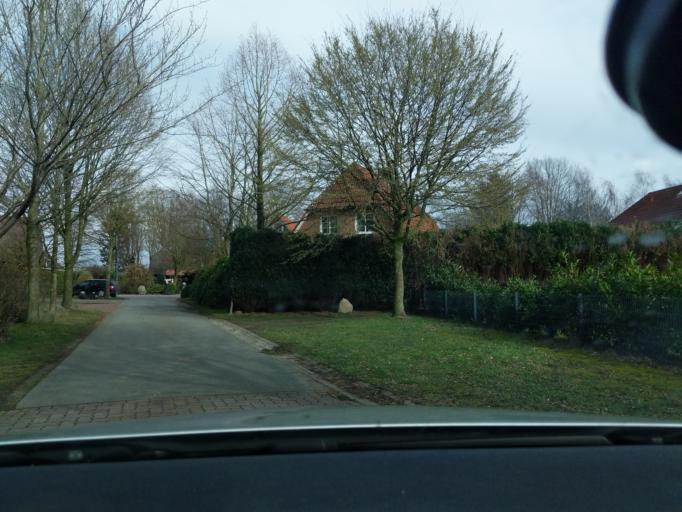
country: DE
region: Lower Saxony
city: Heinbockel
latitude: 53.5718
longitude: 9.3303
